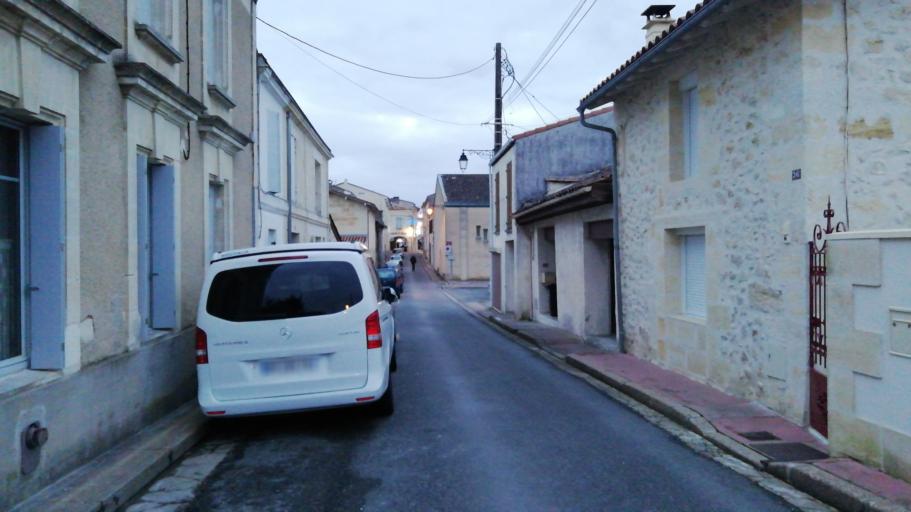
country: FR
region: Aquitaine
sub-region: Departement de la Gironde
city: Creon
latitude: 44.7739
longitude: -0.3497
